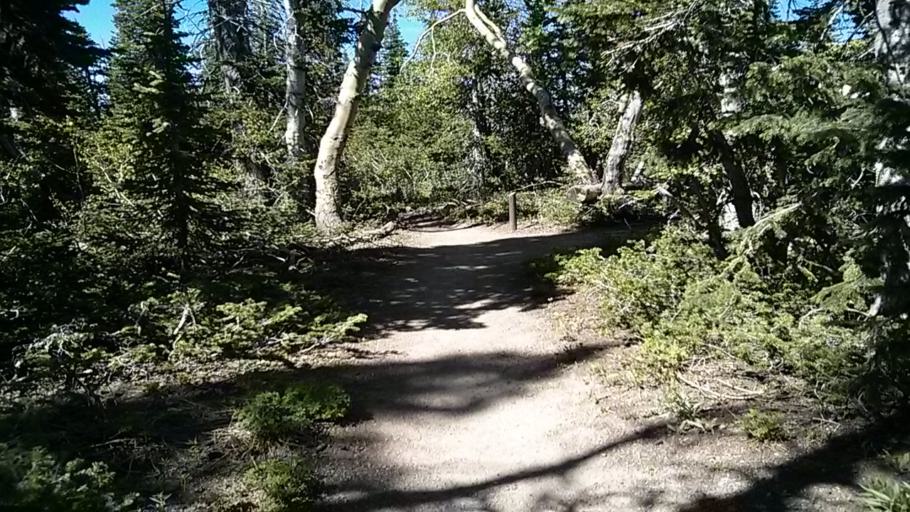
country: US
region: Utah
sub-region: Iron County
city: Parowan
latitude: 37.6349
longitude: -112.8255
